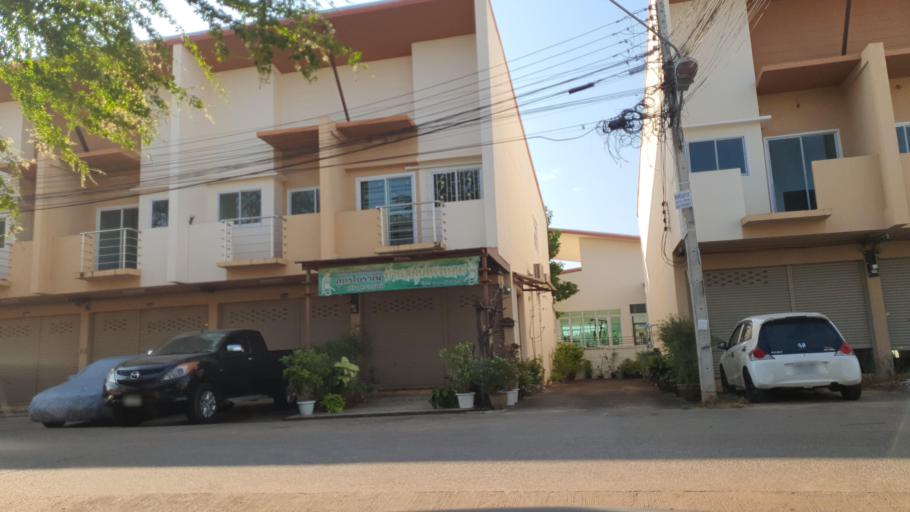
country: TH
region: Khon Kaen
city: Khon Kaen
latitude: 16.4204
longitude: 102.8131
